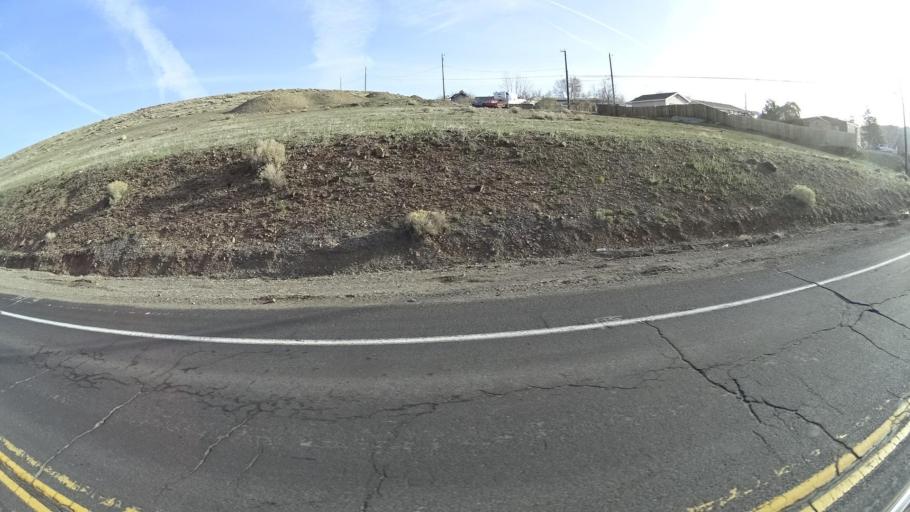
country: US
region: Nevada
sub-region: Washoe County
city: Sun Valley
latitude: 39.5706
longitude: -119.7859
